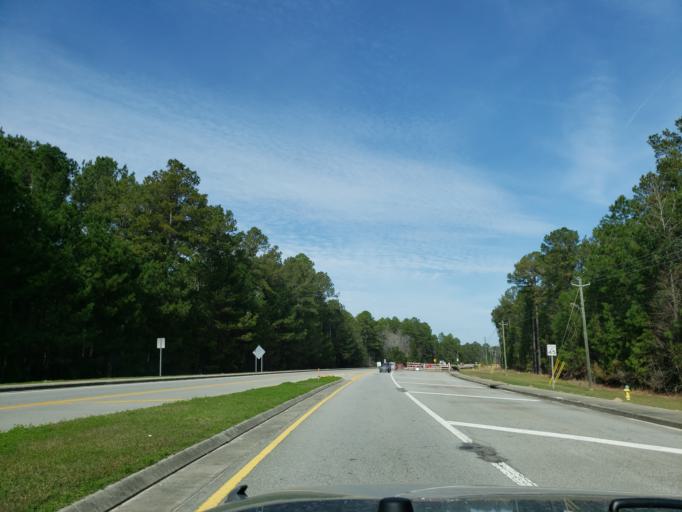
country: US
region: Georgia
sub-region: Chatham County
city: Pooler
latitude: 32.1674
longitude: -81.2340
